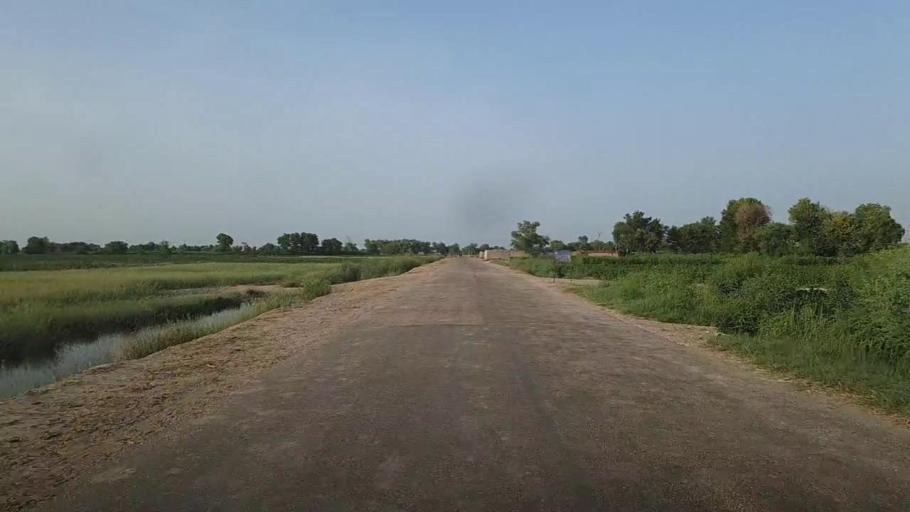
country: PK
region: Sindh
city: Ubauro
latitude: 28.1205
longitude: 69.8258
